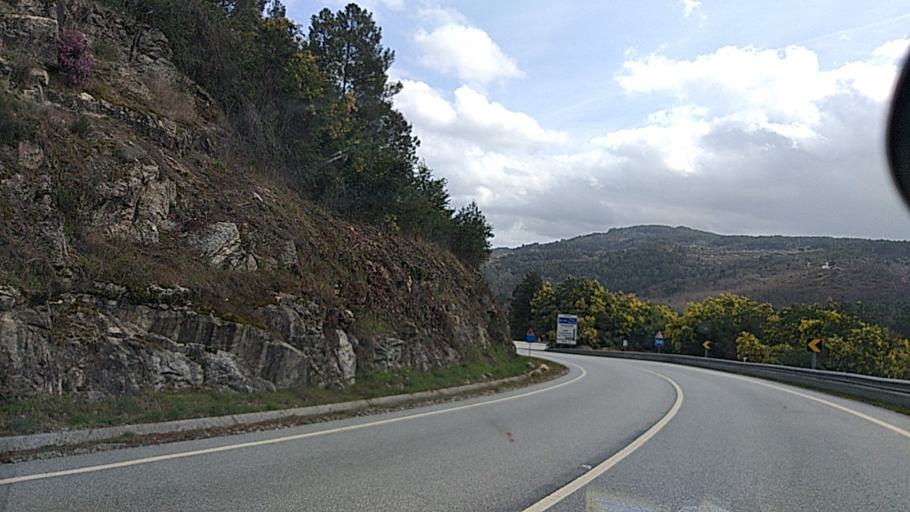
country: PT
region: Viseu
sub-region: Mangualde
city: Mangualde
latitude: 40.6473
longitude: -7.7314
